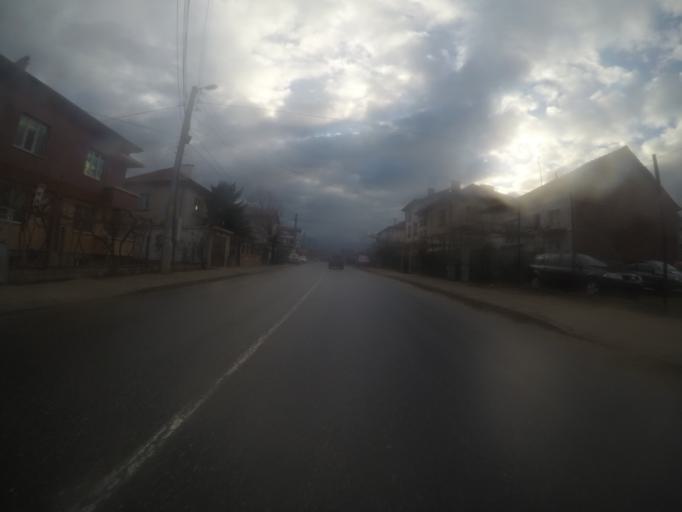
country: BG
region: Blagoevgrad
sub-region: Obshtina Simitli
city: Simitli
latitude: 41.8816
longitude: 23.1227
